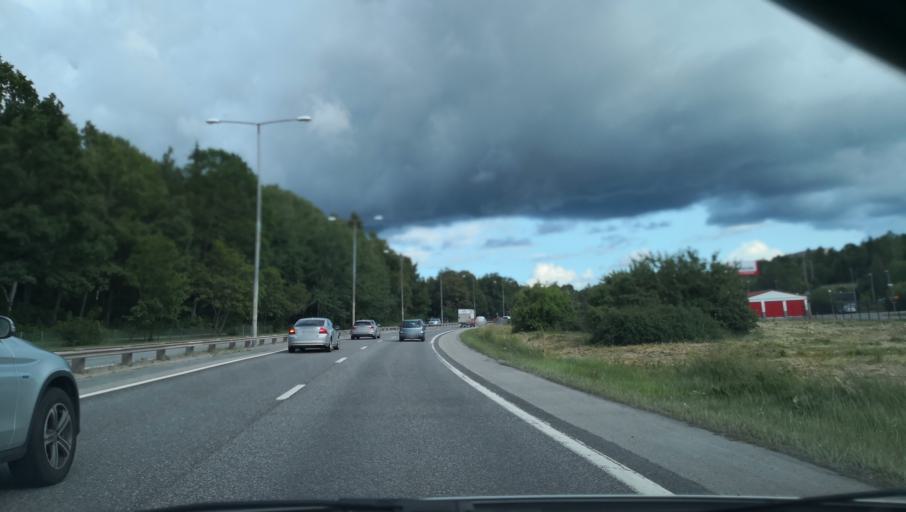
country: SE
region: Stockholm
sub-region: Stockholms Kommun
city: Arsta
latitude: 59.2623
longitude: 18.0316
